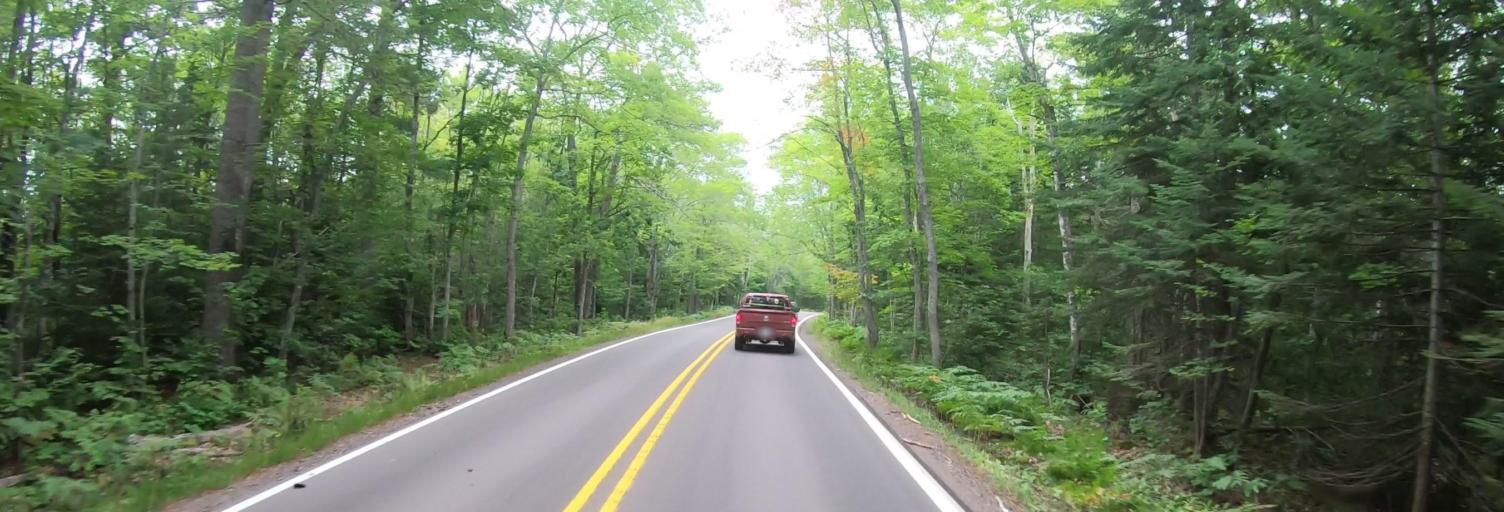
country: US
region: Michigan
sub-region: Keweenaw County
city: Eagle River
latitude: 47.4434
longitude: -87.9406
